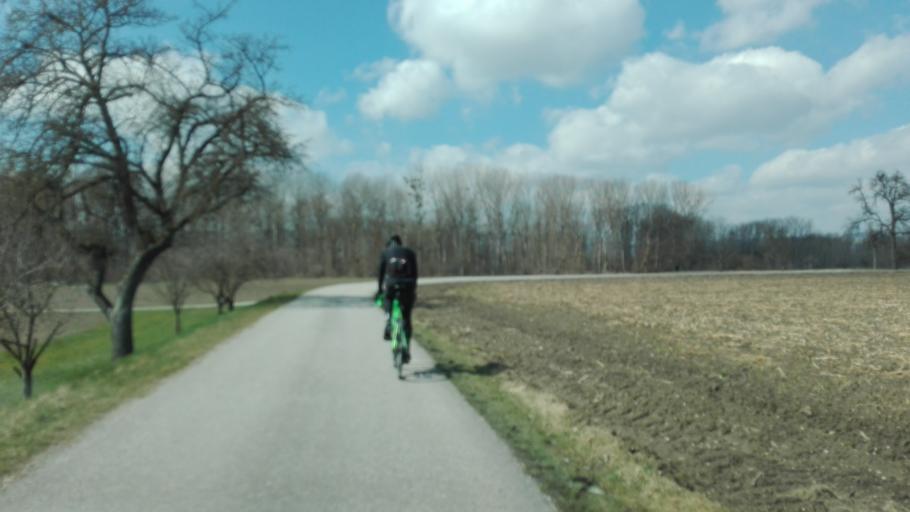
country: AT
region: Upper Austria
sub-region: Politischer Bezirk Urfahr-Umgebung
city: Feldkirchen an der Donau
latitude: 48.3421
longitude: 14.0338
